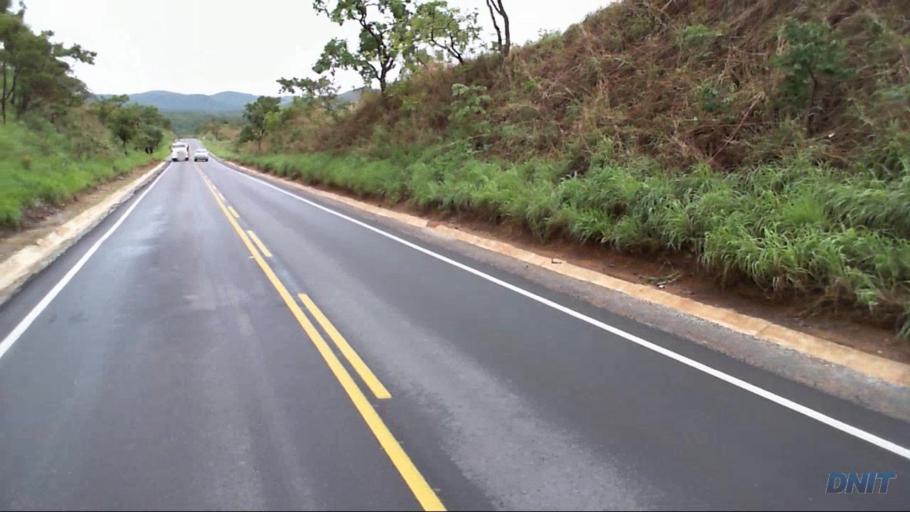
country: BR
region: Goias
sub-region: Padre Bernardo
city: Padre Bernardo
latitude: -15.4909
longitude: -48.2289
